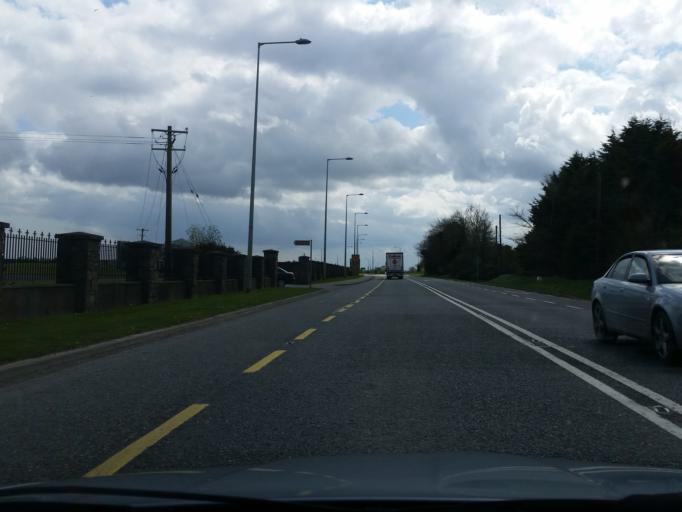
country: IE
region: Leinster
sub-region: An Mhi
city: Ashbourne
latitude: 53.5296
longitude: -6.4191
